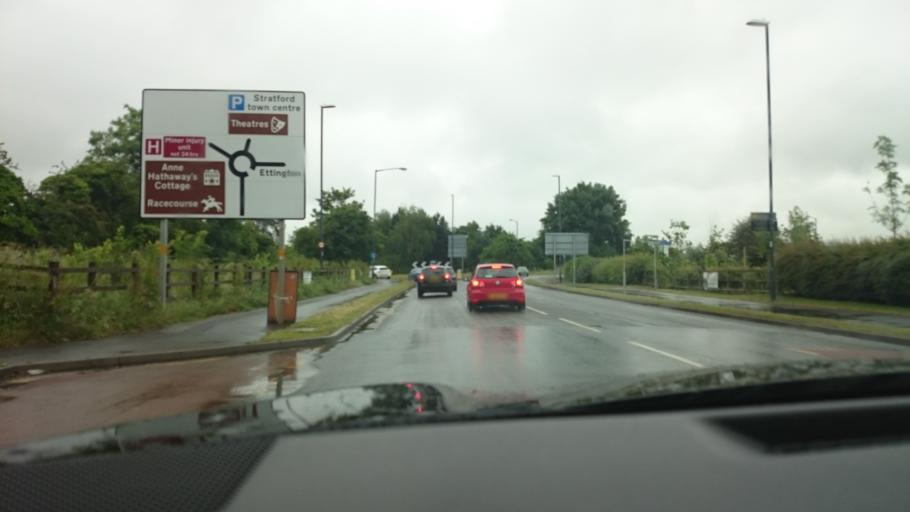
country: GB
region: England
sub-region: Warwickshire
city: Stratford-upon-Avon
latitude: 52.1803
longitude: -1.7006
